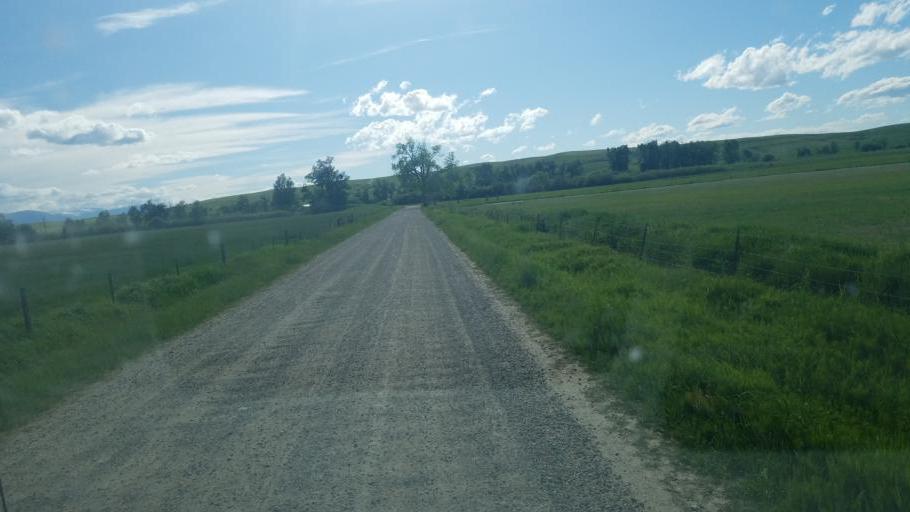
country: US
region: Montana
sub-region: Carbon County
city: Red Lodge
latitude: 45.3636
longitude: -109.1751
